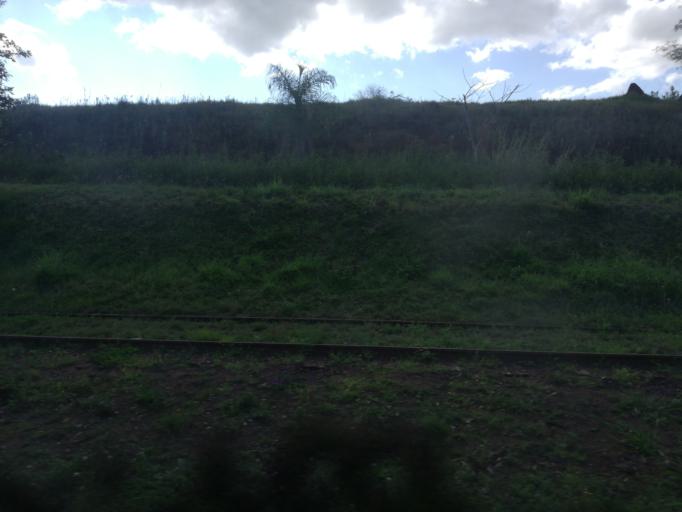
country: PY
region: Itapua
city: Encarnacion
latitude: -27.3655
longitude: -55.8531
